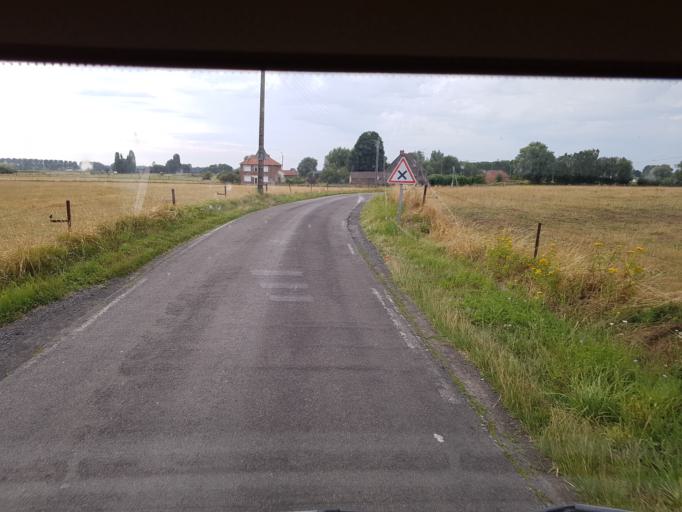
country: FR
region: Nord-Pas-de-Calais
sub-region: Departement du Nord
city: Vieux-Conde
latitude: 50.4833
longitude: 3.5599
